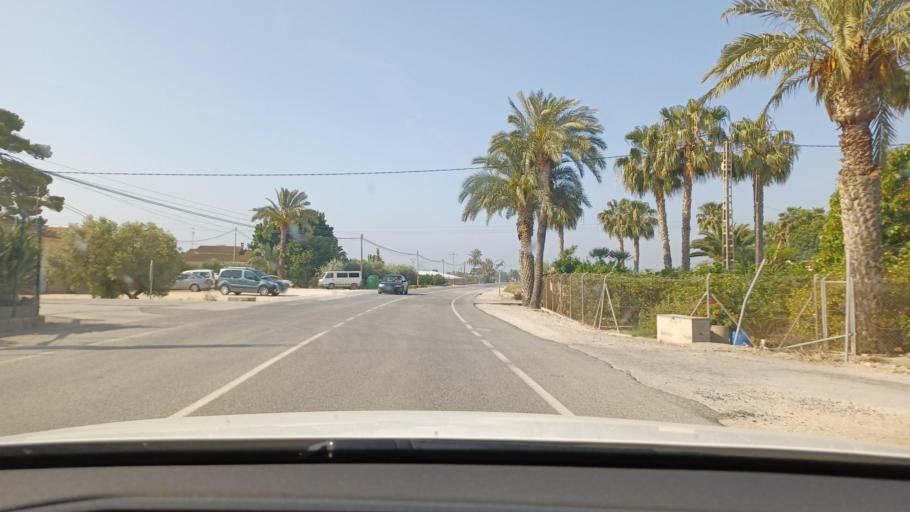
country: ES
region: Valencia
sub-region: Provincia de Alicante
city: Elche
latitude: 38.2218
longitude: -0.7195
